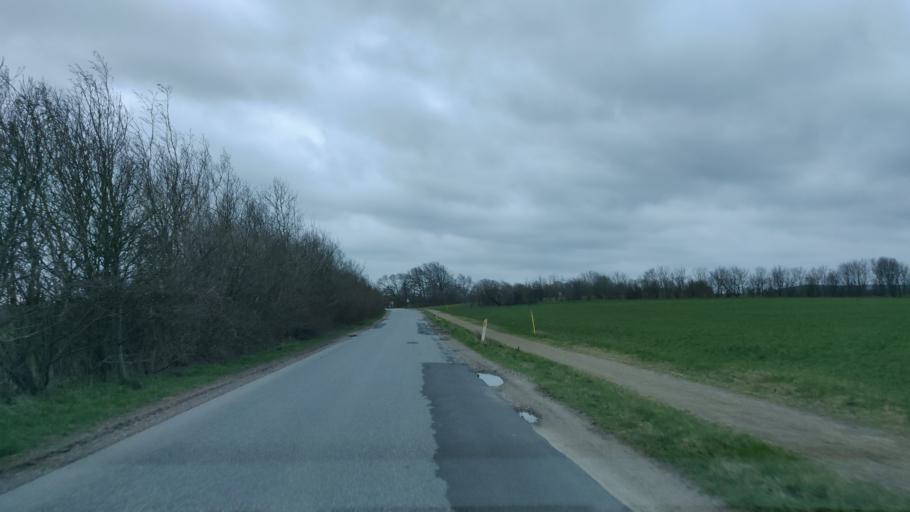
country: DK
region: Central Jutland
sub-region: Viborg Kommune
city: Stoholm
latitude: 56.4925
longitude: 9.1754
